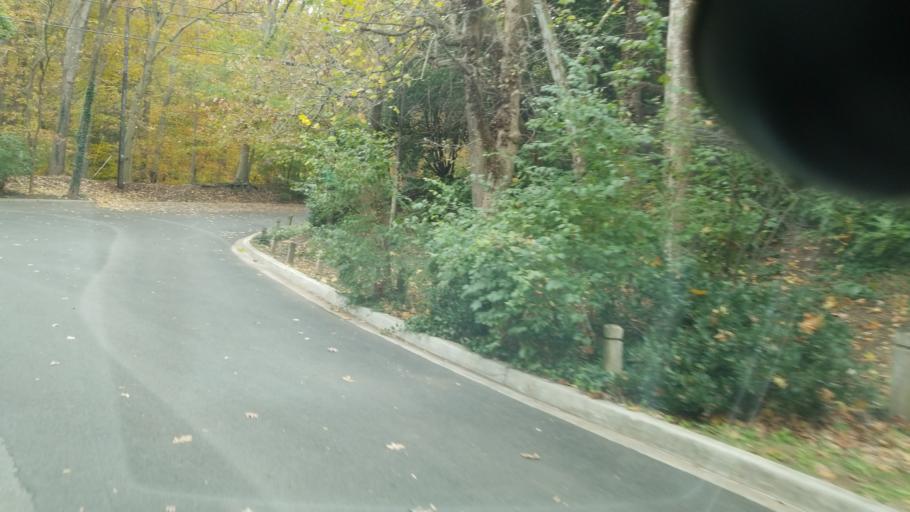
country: US
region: Maryland
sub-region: Montgomery County
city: Chevy Chase
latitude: 38.9467
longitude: -77.0591
